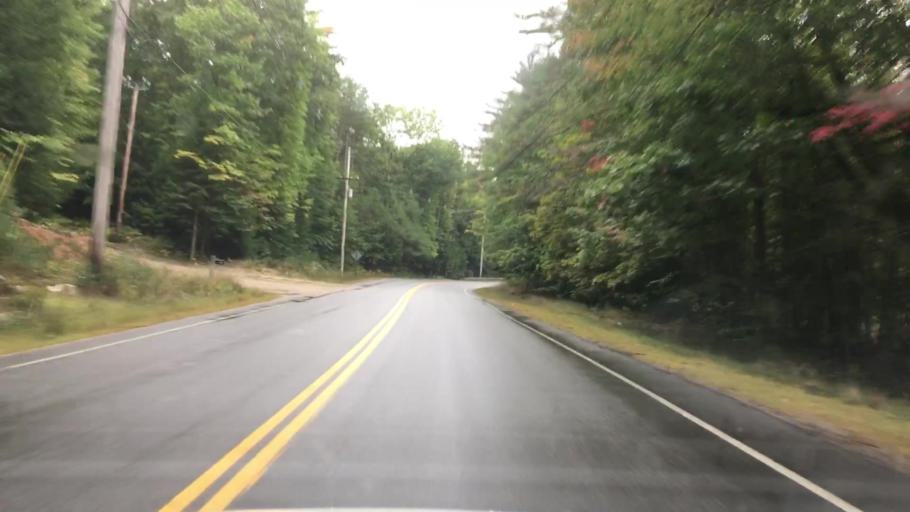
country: US
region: Maine
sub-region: Cumberland County
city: Raymond
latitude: 43.9809
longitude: -70.5236
